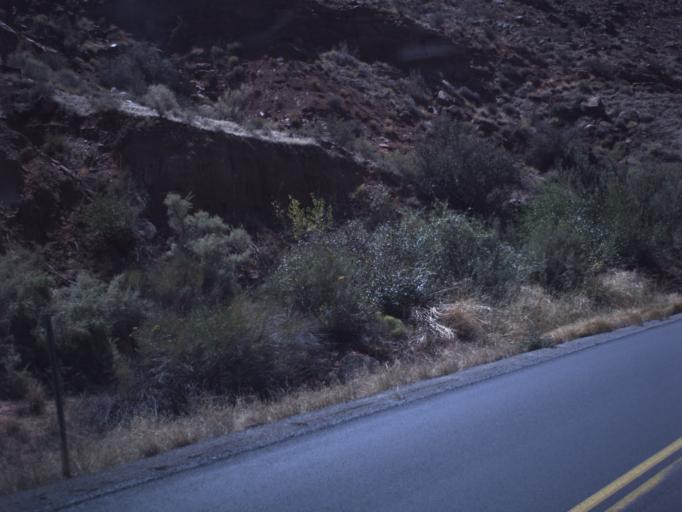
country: US
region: Utah
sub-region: Grand County
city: Moab
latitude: 38.6324
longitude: -109.4871
